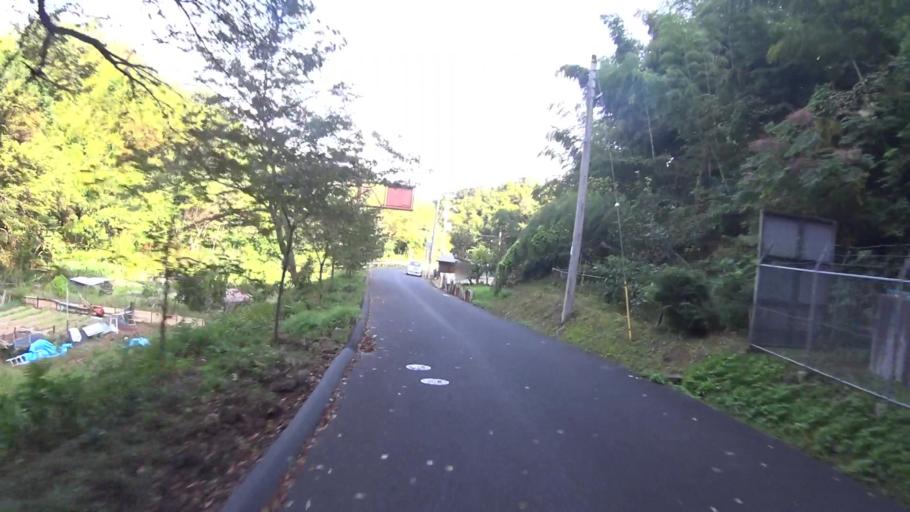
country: JP
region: Kyoto
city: Miyazu
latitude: 35.5642
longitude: 135.1412
